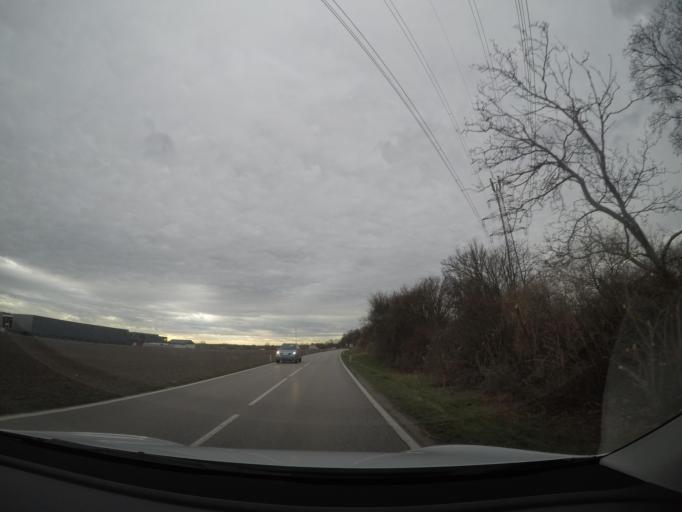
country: AT
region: Lower Austria
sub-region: Politischer Bezirk Modling
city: Biedermannsdorf
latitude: 48.0848
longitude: 16.3593
